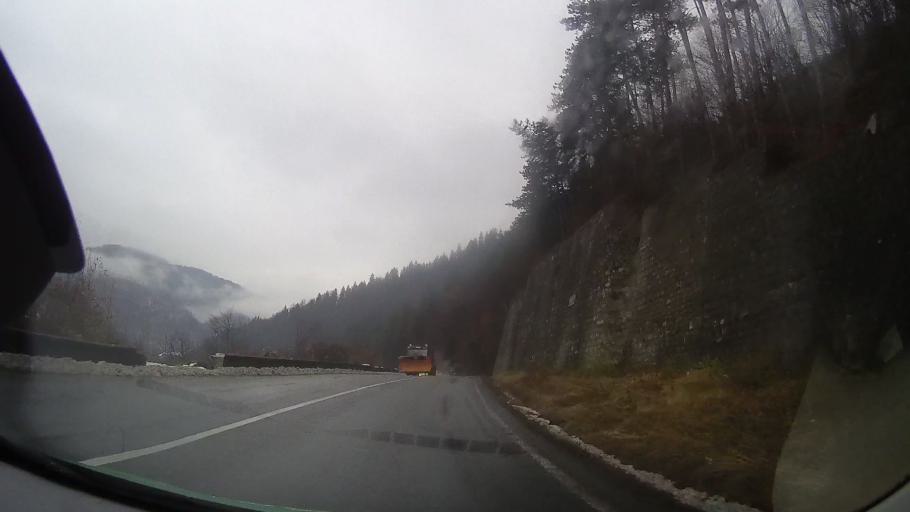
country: RO
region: Neamt
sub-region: Comuna Tarcau
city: Tarcau
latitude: 46.8931
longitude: 26.1364
